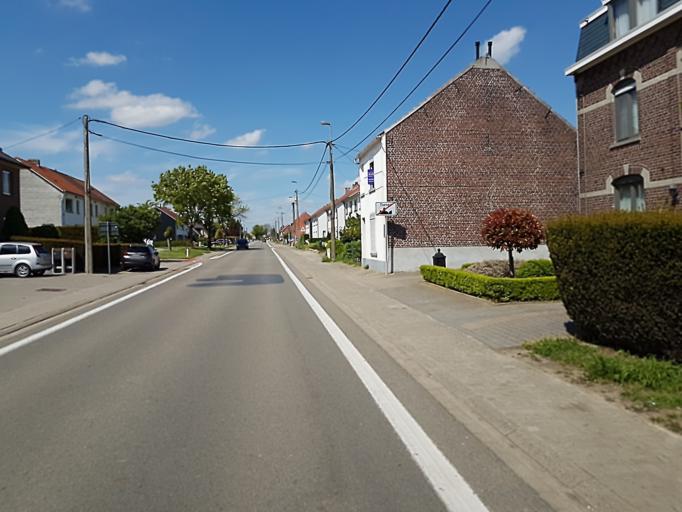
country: BE
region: Flanders
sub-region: Provincie Vlaams-Brabant
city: Tienen
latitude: 50.8228
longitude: 4.9246
